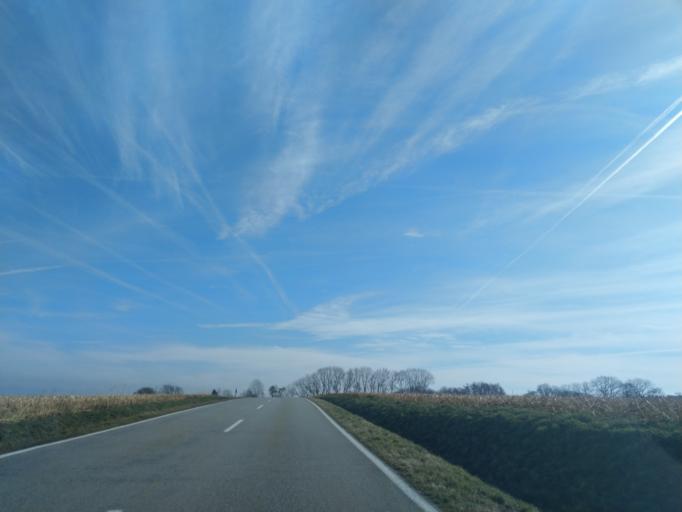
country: DE
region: Bavaria
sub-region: Lower Bavaria
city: Buchhofen
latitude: 48.6773
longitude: 12.9096
